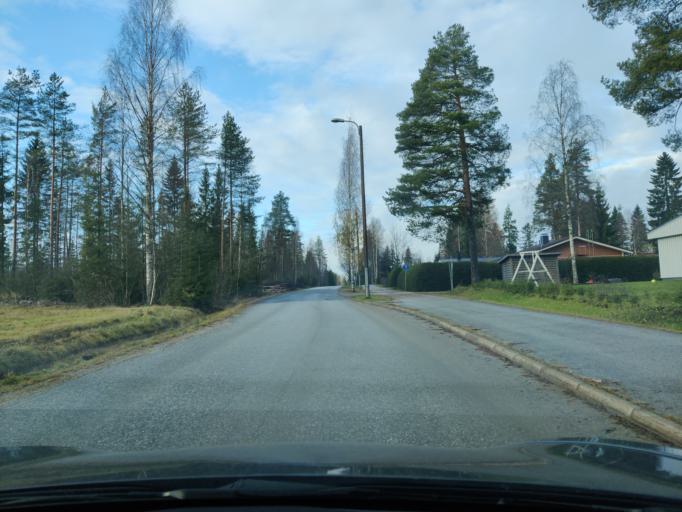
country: FI
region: Northern Savo
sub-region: Ylae-Savo
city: Kiuruvesi
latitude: 63.6435
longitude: 26.6390
